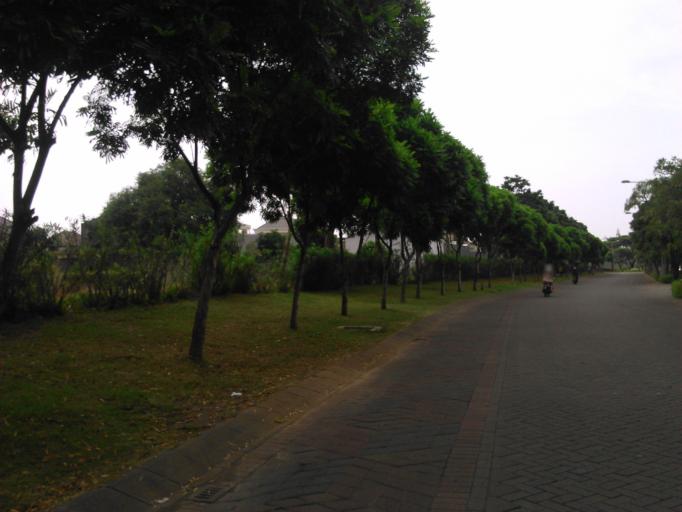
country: ID
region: East Java
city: Semampir
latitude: -7.2869
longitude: 112.7877
